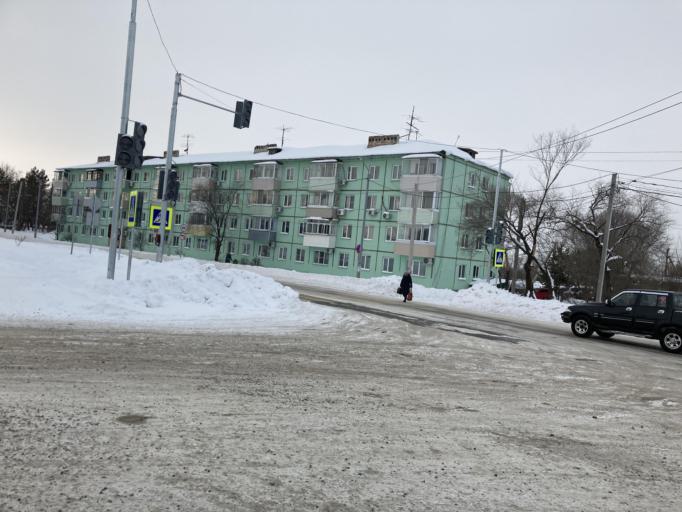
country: RU
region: Khabarovsk Krai
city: Khor
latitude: 47.9655
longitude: 135.0534
